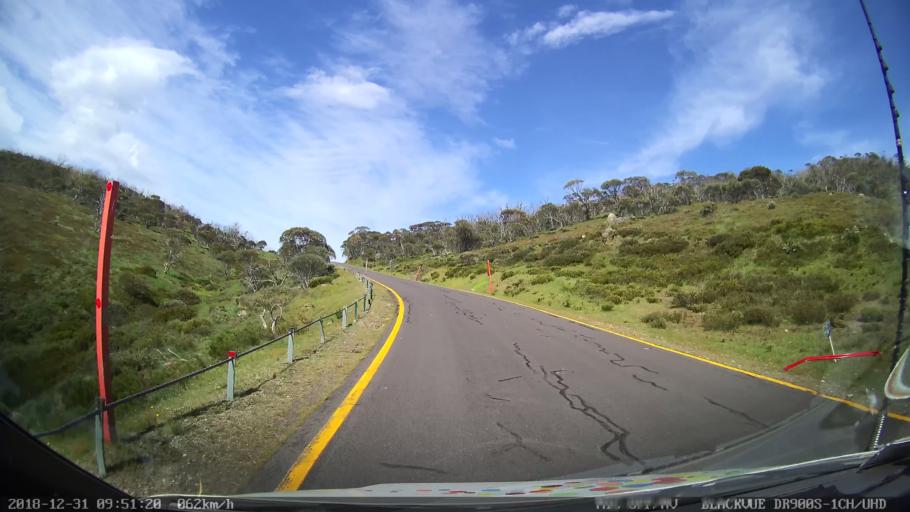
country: AU
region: New South Wales
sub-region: Snowy River
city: Jindabyne
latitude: -36.5226
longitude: 148.2630
